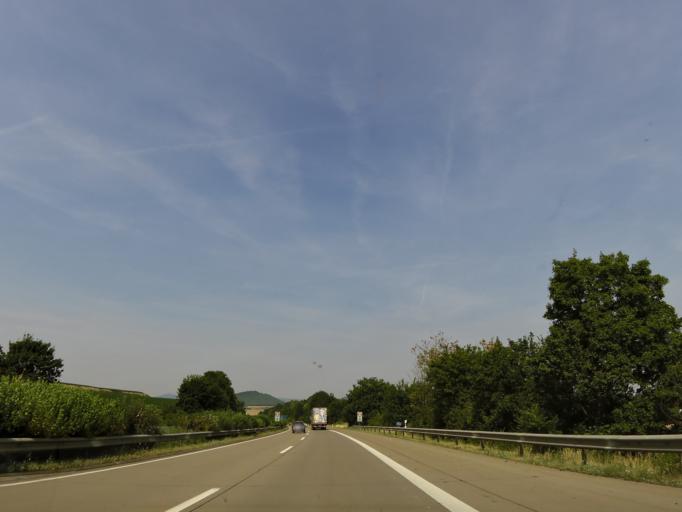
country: DE
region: Rheinland-Pfalz
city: Saffig
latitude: 50.3766
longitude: 7.4060
